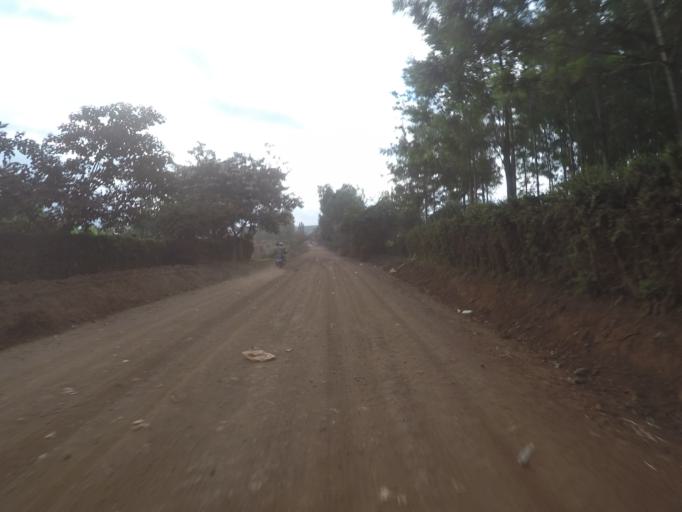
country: TZ
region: Arusha
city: Kiratu
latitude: -3.3240
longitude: 35.6652
